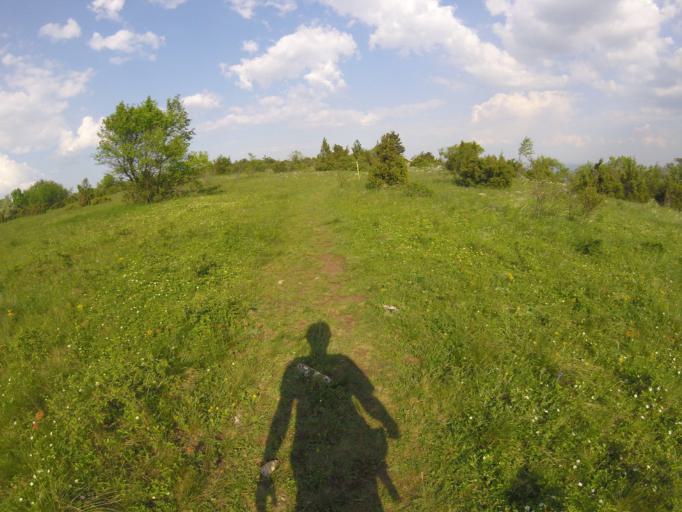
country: SK
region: Kosicky
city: Medzev
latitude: 48.6188
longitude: 20.8484
